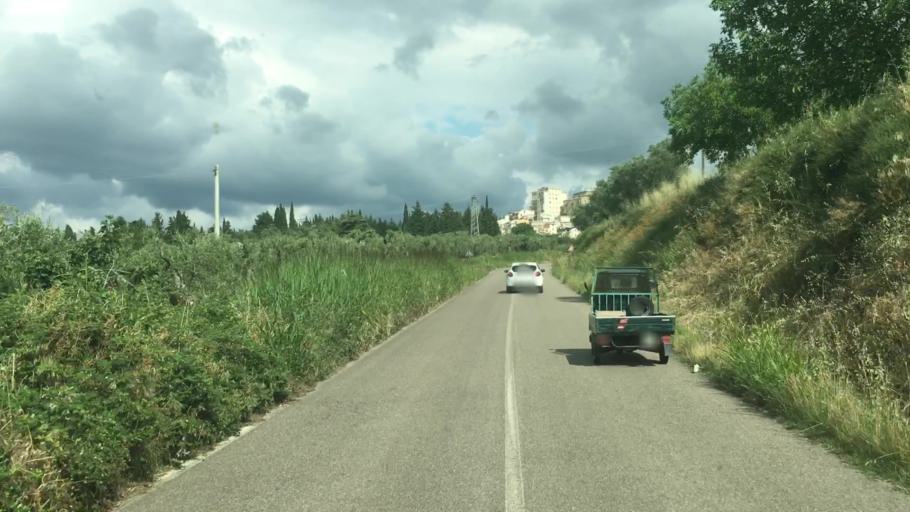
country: IT
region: Basilicate
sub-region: Provincia di Matera
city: San Mauro Forte
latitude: 40.4818
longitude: 16.2589
